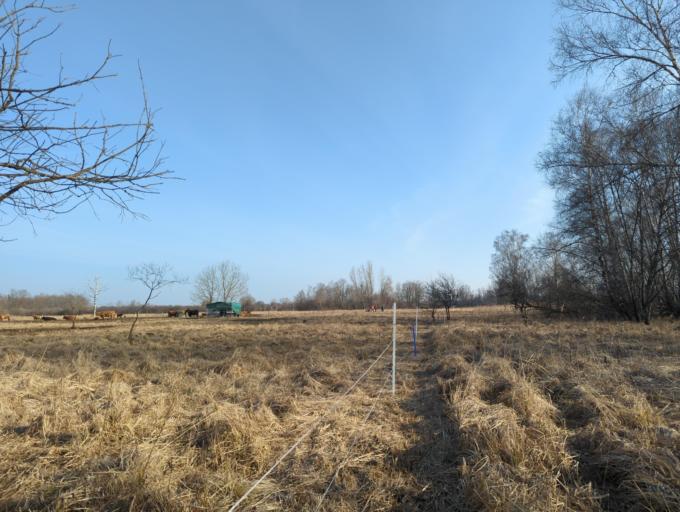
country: DE
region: Bavaria
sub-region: Swabia
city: Leipheim
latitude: 48.4791
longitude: 10.2055
